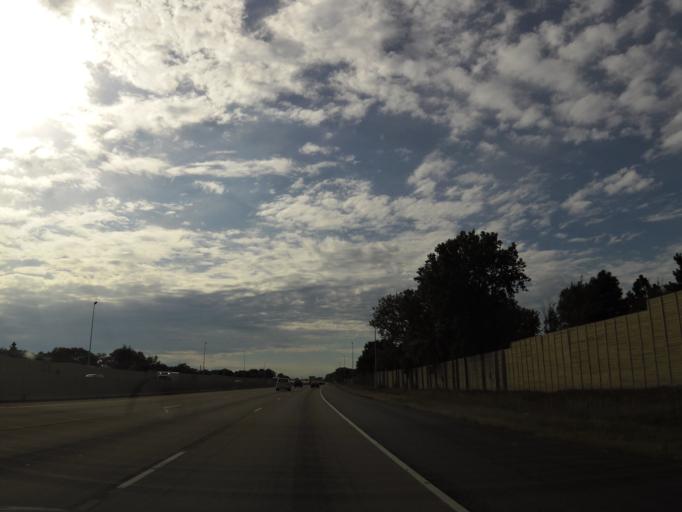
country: US
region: Minnesota
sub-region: Hennepin County
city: Brooklyn Park
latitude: 45.0765
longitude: -93.3579
